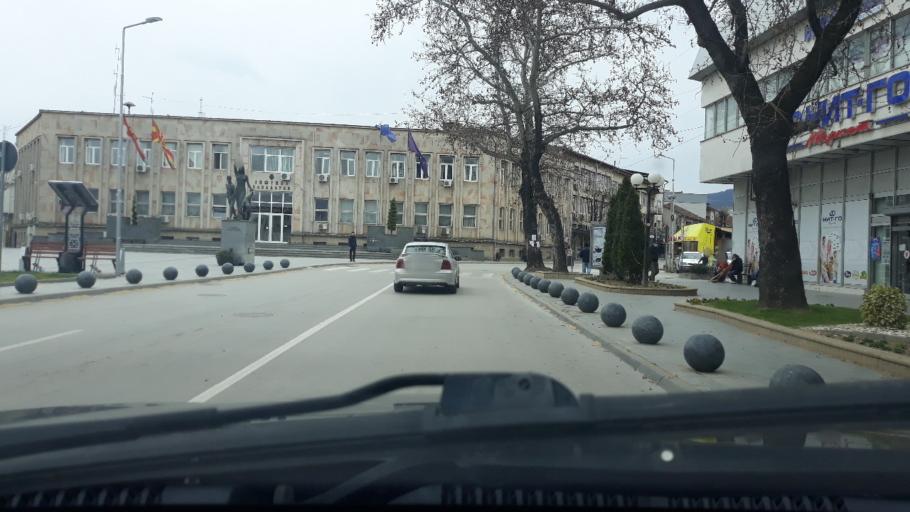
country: MK
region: Kavadarci
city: Kavadarci
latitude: 41.4334
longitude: 22.0119
